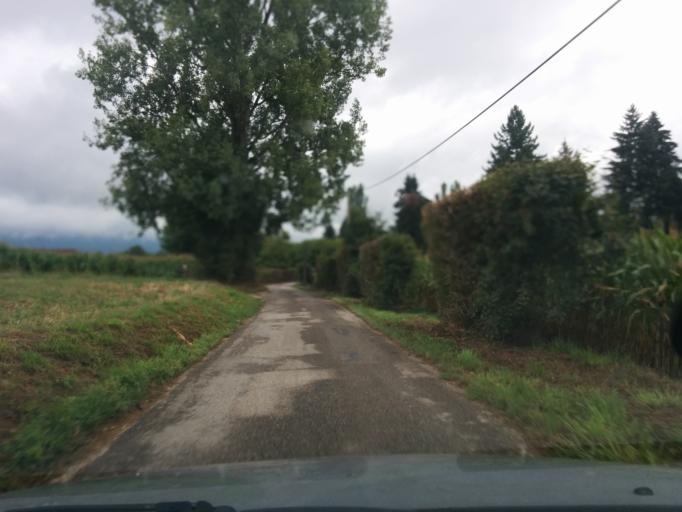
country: FR
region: Rhone-Alpes
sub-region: Departement de la Savoie
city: Le Pont-de-Beauvoisin
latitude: 45.5449
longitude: 5.6592
